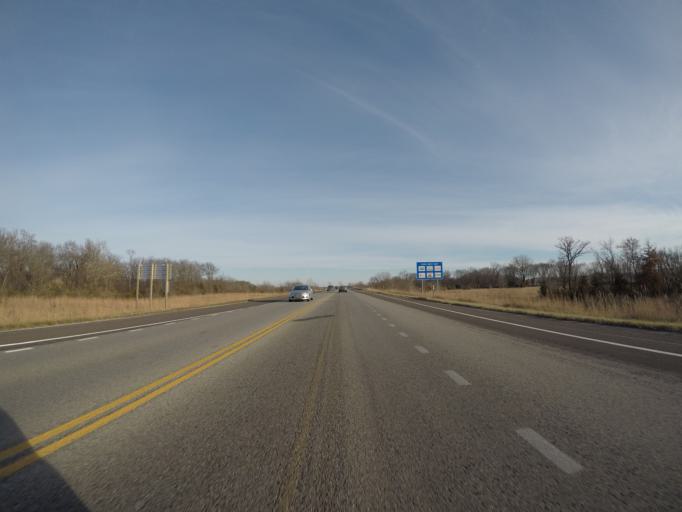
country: US
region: Kansas
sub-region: Douglas County
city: Lawrence
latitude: 38.9214
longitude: -95.2759
